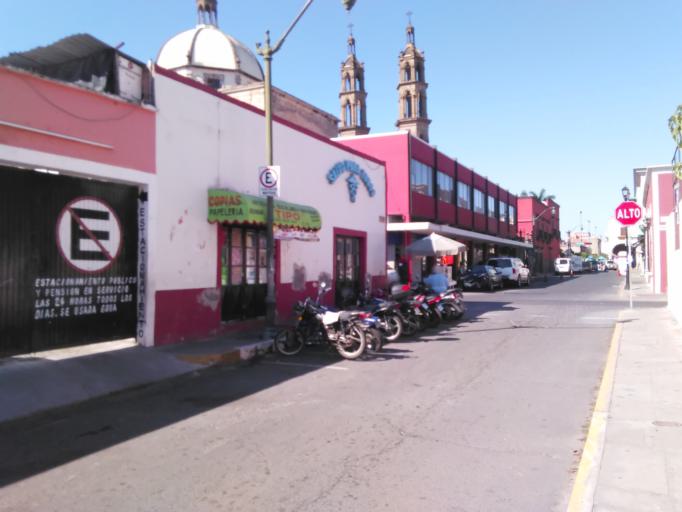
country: MX
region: Nayarit
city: Tepic
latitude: 21.5119
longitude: -104.8904
